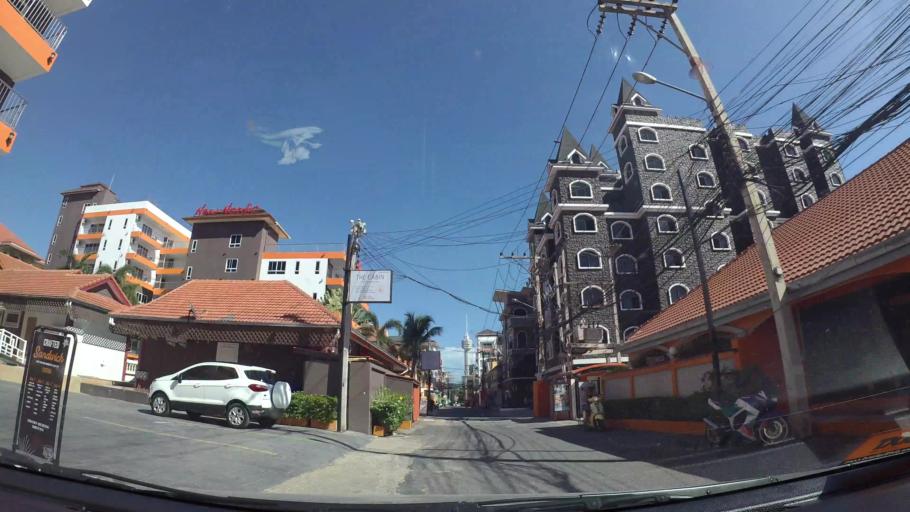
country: TH
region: Chon Buri
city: Phatthaya
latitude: 12.9161
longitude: 100.8623
